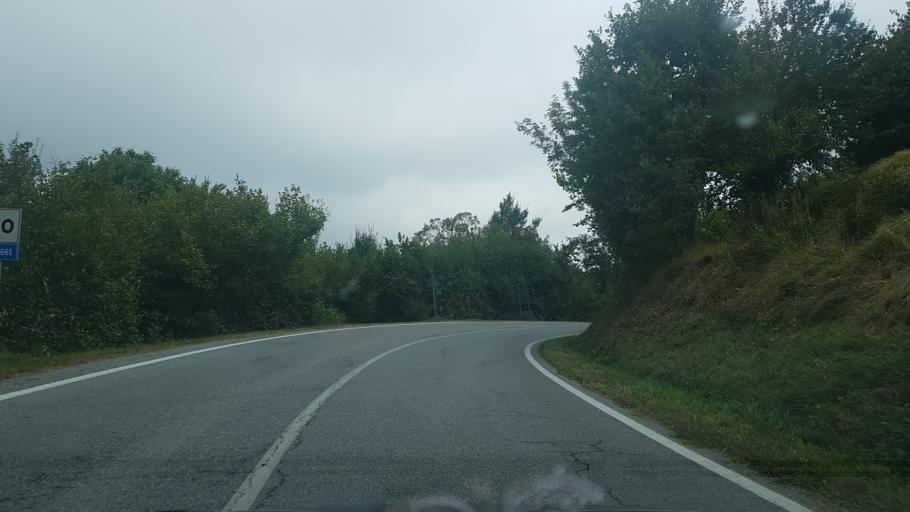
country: IT
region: Piedmont
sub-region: Provincia di Cuneo
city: Sale San Giovanni
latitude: 44.4177
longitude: 8.0892
